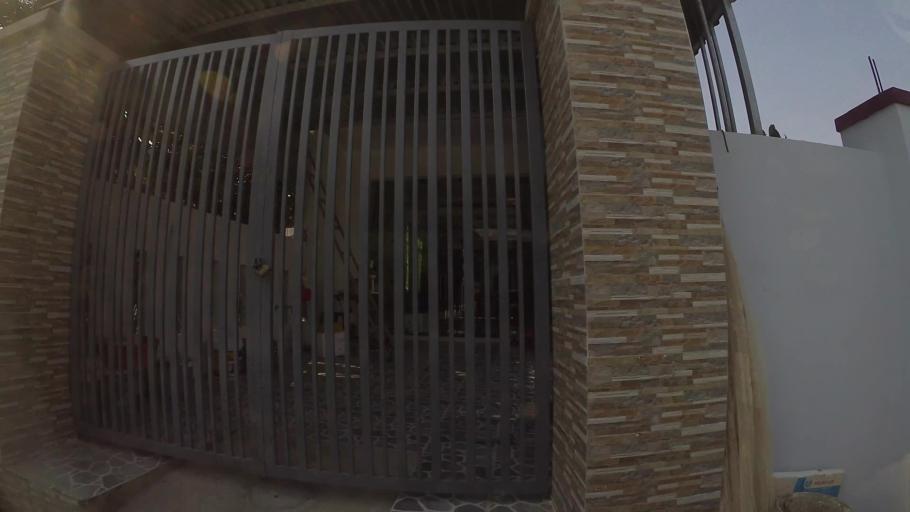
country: VN
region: Quang Nam
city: Quang Nam
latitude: 15.9471
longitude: 108.2564
